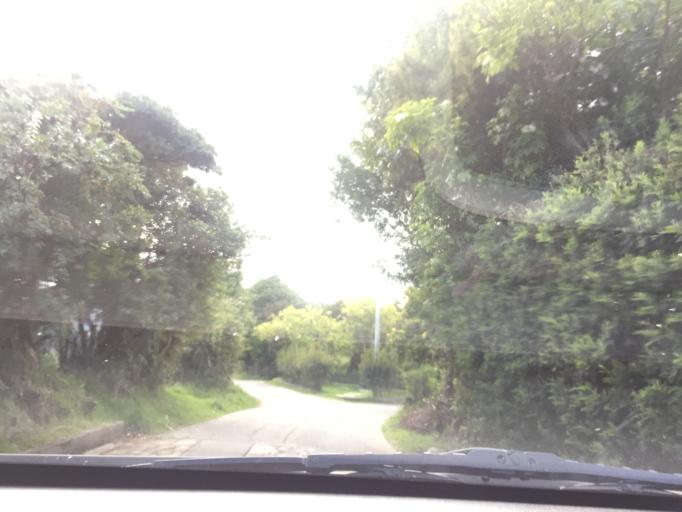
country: CO
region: Cundinamarca
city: Sopo
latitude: 4.9135
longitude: -73.9284
